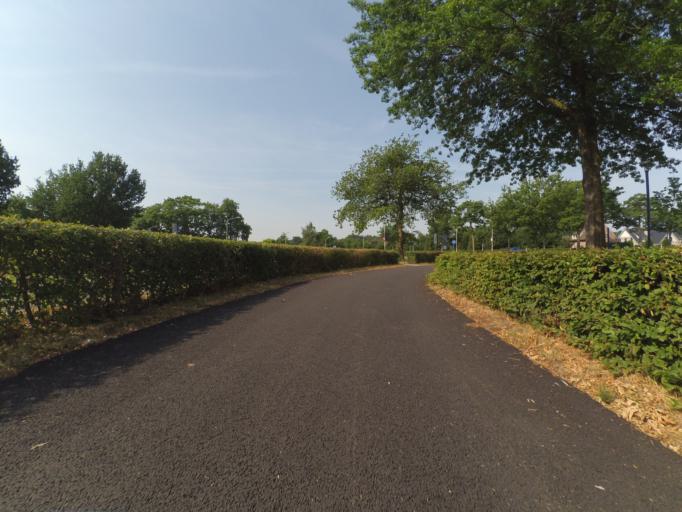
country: NL
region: North Brabant
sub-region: Gemeente Woensdrecht
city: Woensdrecht
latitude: 51.4172
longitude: 4.3356
